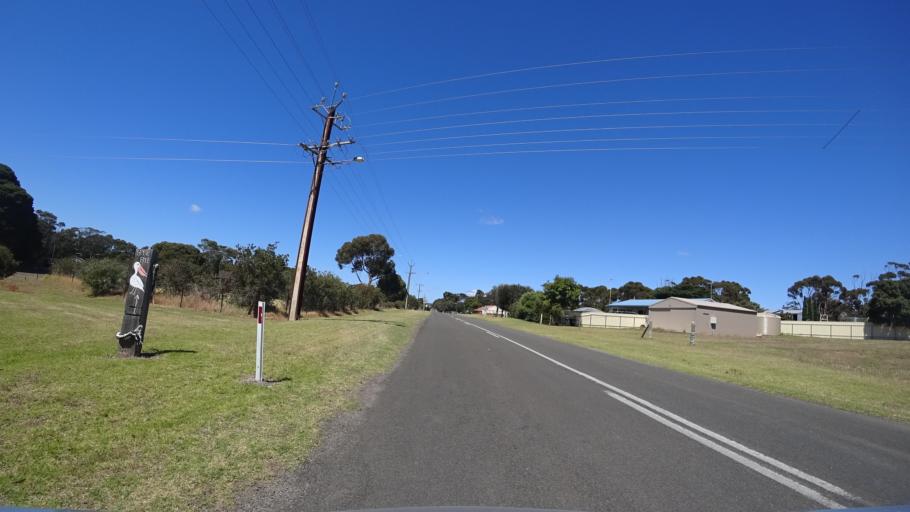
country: AU
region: South Australia
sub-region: Kangaroo Island
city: Kingscote
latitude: -35.7816
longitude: 137.7707
